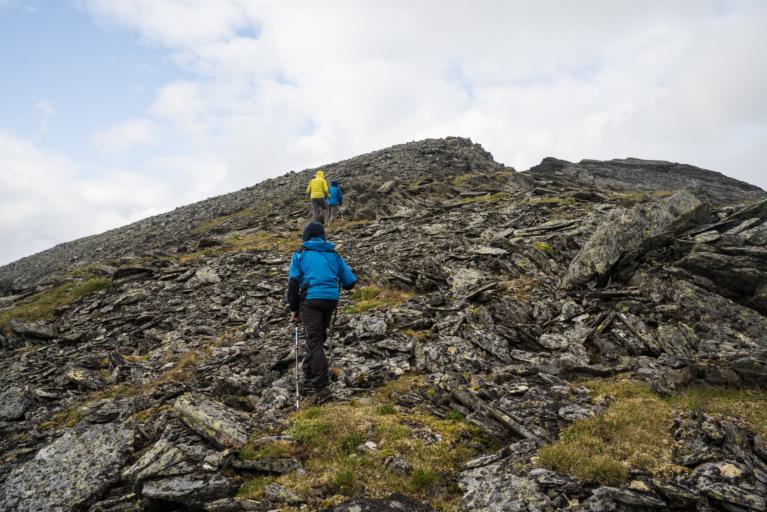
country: RU
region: Komi Republic
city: Synya
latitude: 64.8273
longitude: 59.2921
